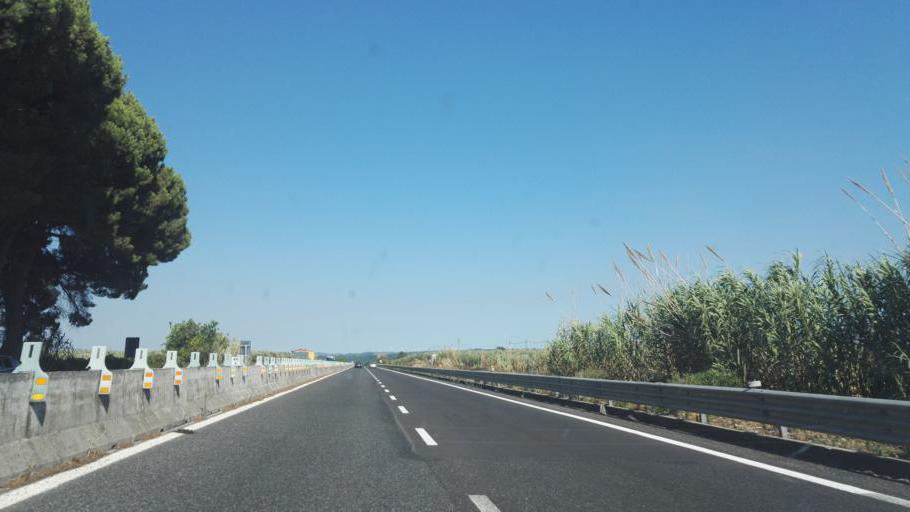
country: IT
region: Calabria
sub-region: Provincia di Catanzaro
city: Santa Eufemia Lamezia
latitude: 38.9131
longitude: 16.2961
